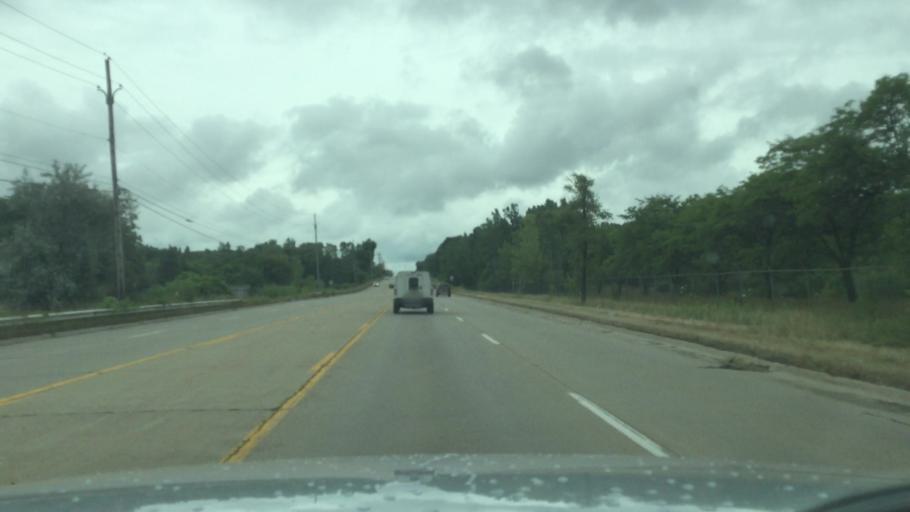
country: US
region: Michigan
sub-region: Genesee County
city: Flushing
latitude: 43.0370
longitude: -83.7737
